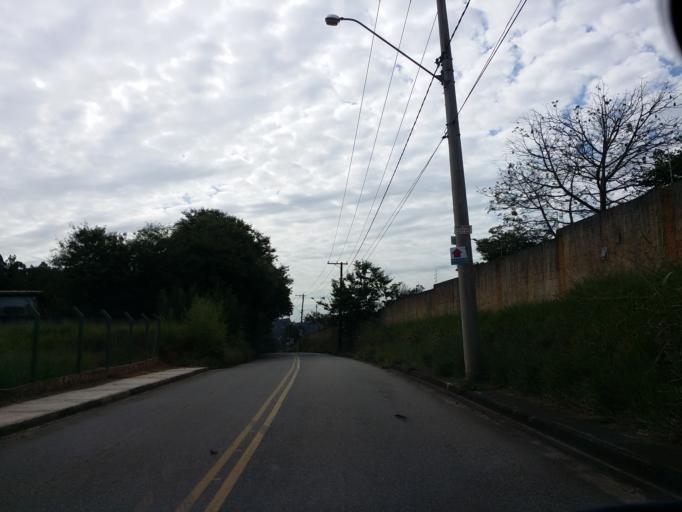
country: BR
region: Sao Paulo
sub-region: Itupeva
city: Itupeva
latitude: -23.2046
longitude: -47.0190
